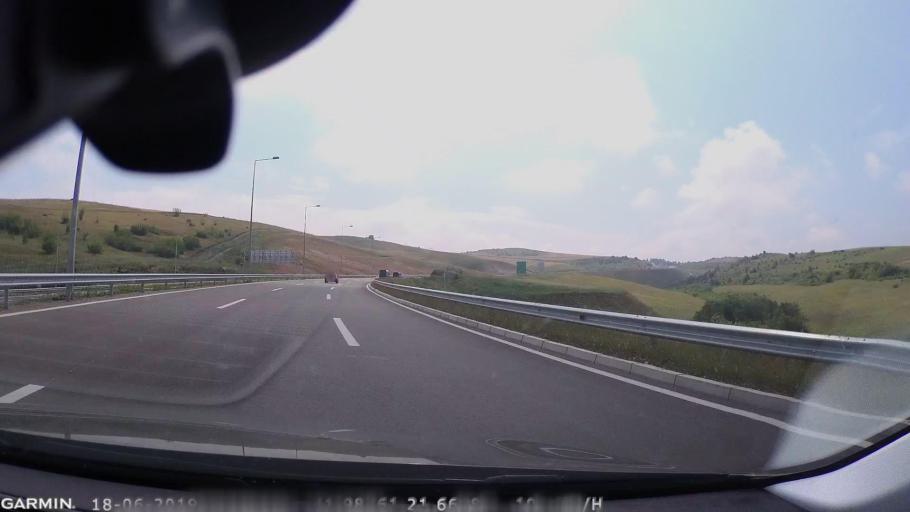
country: MK
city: Miladinovci
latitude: 41.9876
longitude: 21.6620
